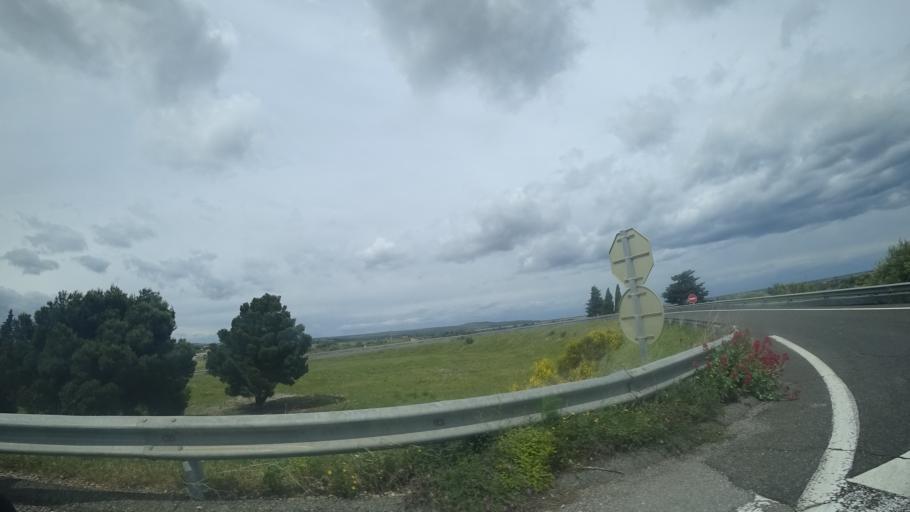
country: FR
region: Languedoc-Roussillon
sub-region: Departement de l'Aude
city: Leucate
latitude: 42.9363
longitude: 2.9920
